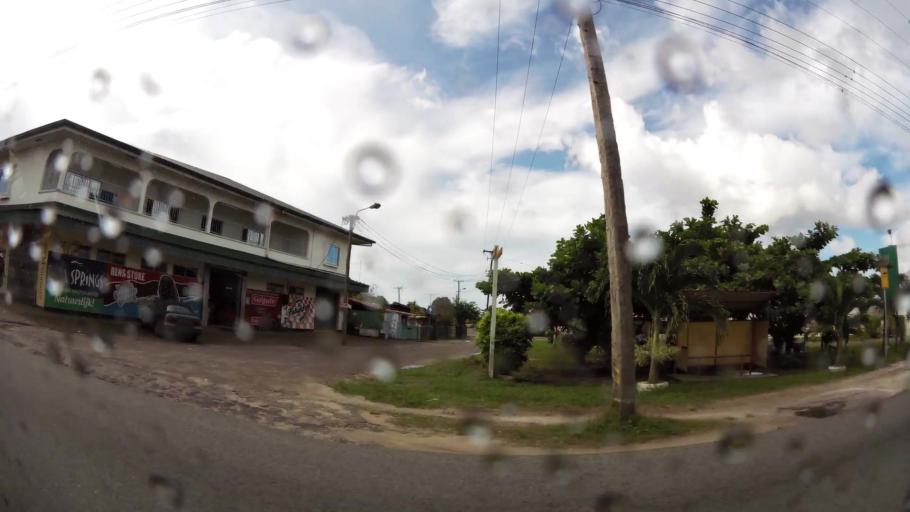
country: SR
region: Paramaribo
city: Paramaribo
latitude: 5.8419
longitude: -55.1961
